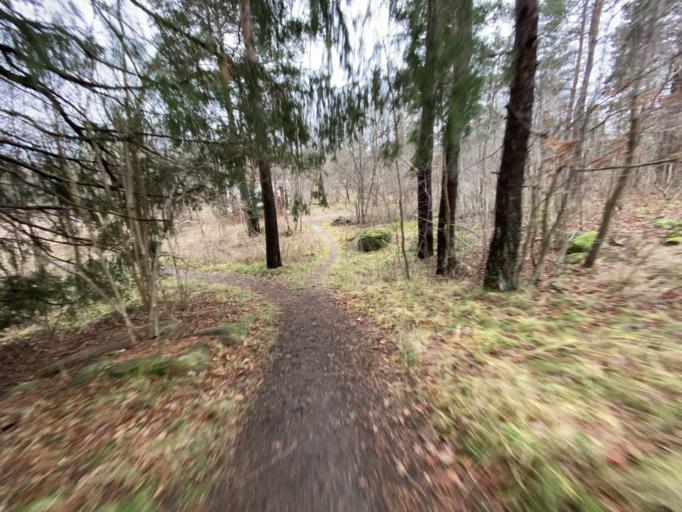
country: SE
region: Vaestra Goetaland
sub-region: Goteborg
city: Eriksbo
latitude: 57.7126
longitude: 12.0465
